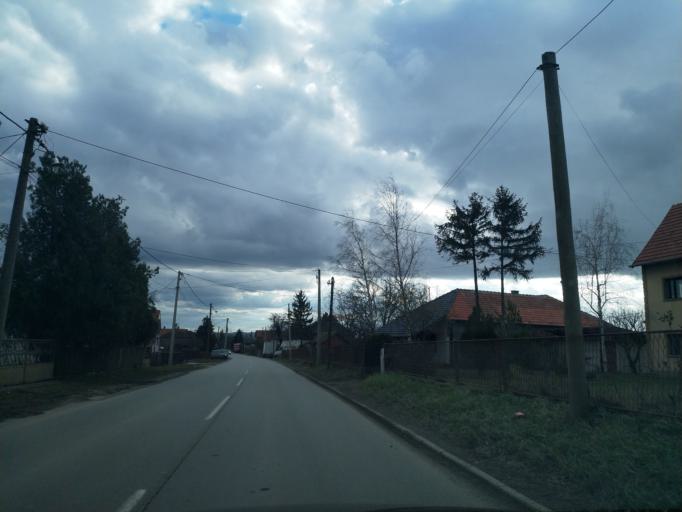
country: RS
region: Central Serbia
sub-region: Belgrade
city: Grocka
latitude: 44.5992
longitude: 20.7256
